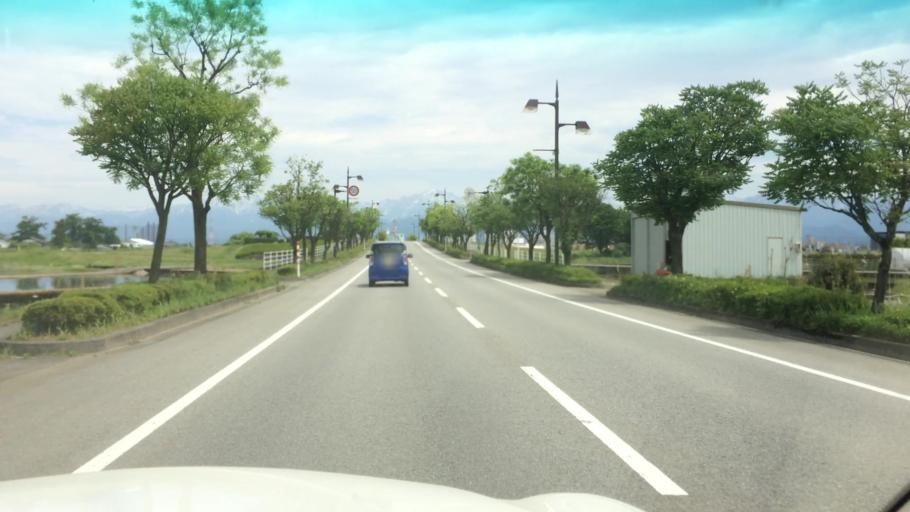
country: JP
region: Toyama
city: Toyama-shi
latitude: 36.6432
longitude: 137.2019
